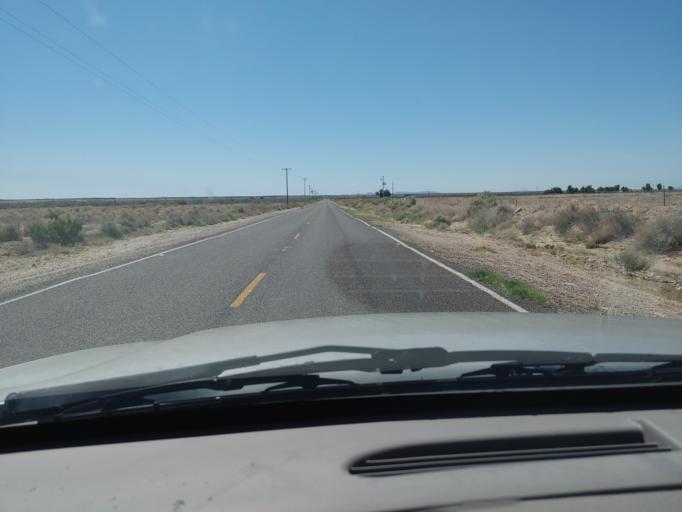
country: US
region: Arizona
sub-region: Maricopa County
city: Gila Bend
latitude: 32.9844
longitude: -113.3059
